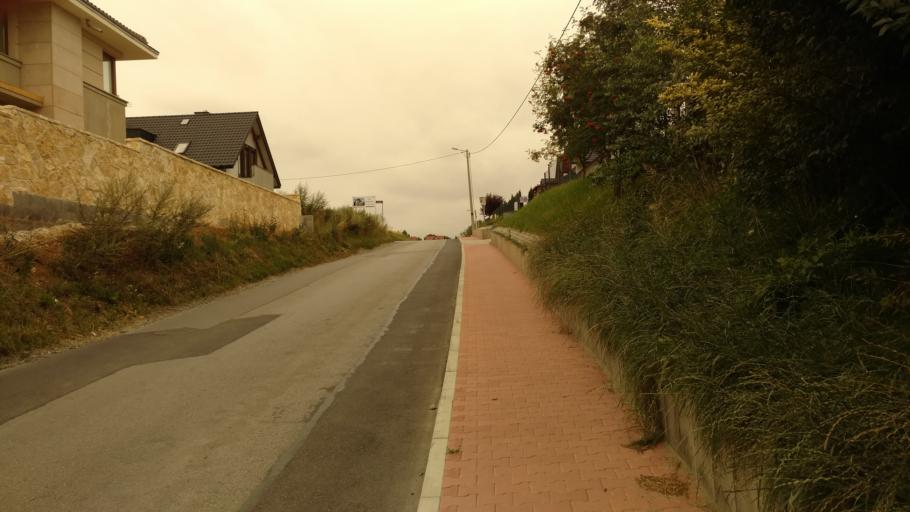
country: PL
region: Lesser Poland Voivodeship
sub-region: Powiat krakowski
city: Michalowice
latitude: 50.1300
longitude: 19.9585
